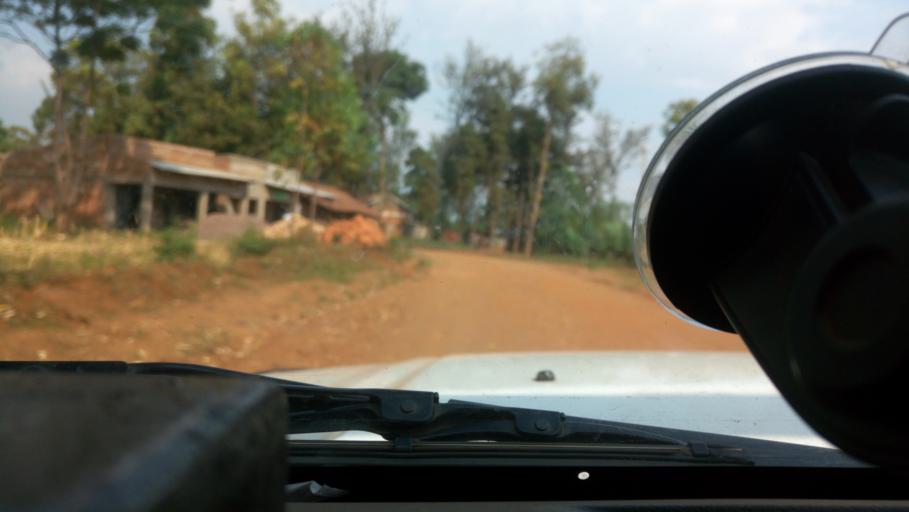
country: KE
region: Kisii
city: Ogembo
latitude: -0.7957
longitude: 34.5953
